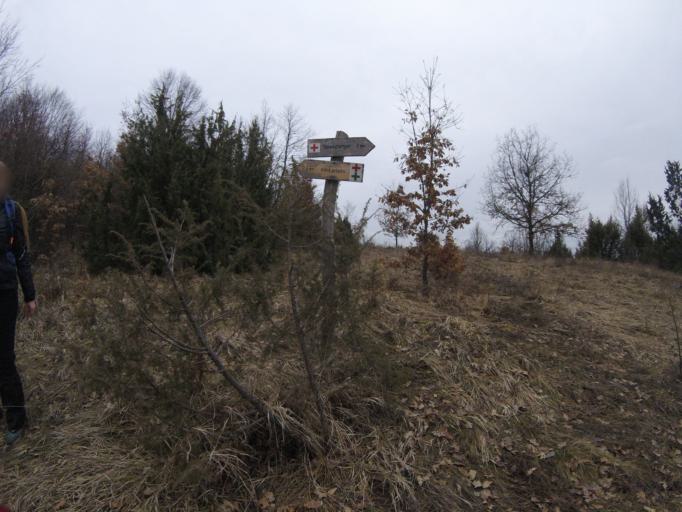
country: HU
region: Borsod-Abauj-Zemplen
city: Rudabanya
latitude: 48.4601
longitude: 20.6093
